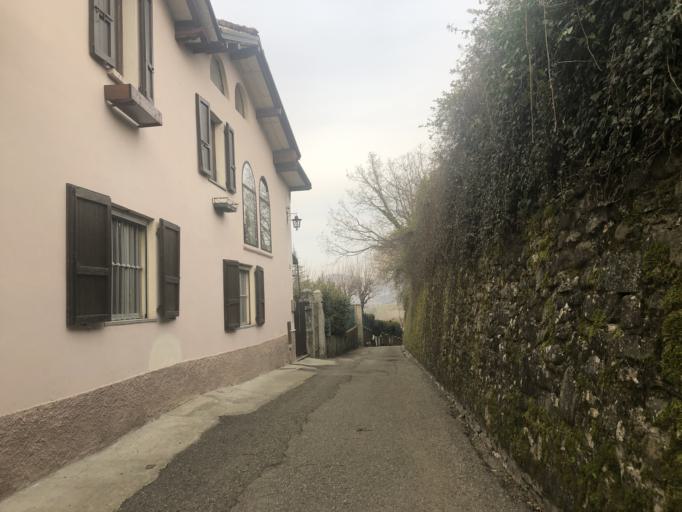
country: IT
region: Emilia-Romagna
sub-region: Provincia di Piacenza
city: Bobbio
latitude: 44.7687
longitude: 9.3836
